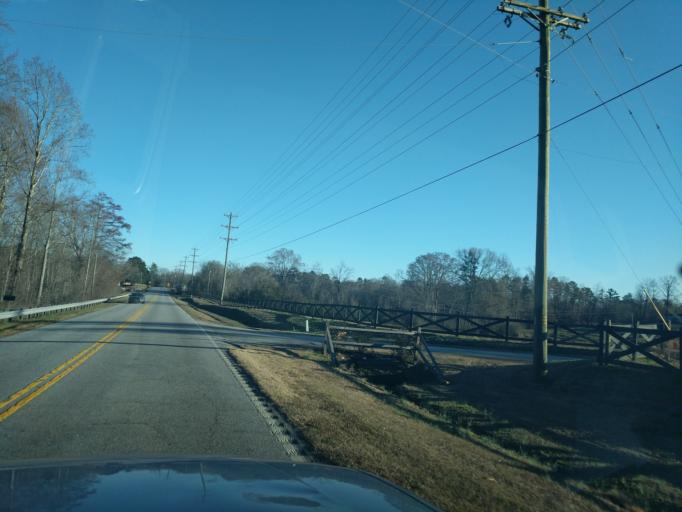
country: US
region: South Carolina
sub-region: Oconee County
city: Westminster
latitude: 34.6931
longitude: -83.1828
